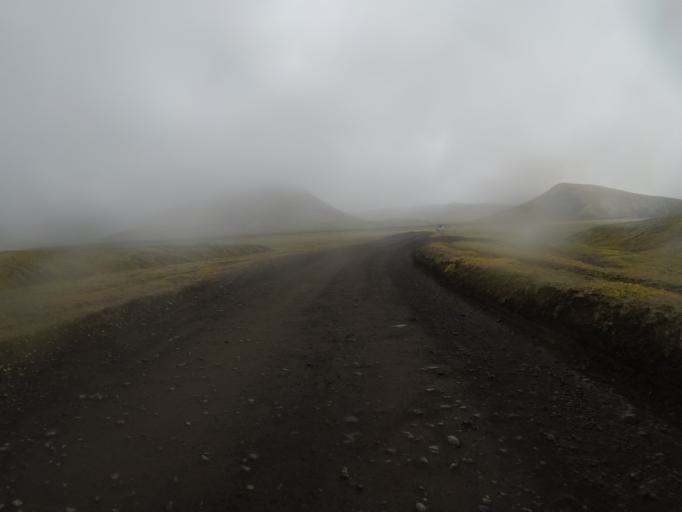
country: IS
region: South
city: Vestmannaeyjar
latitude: 63.9701
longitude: -18.8054
